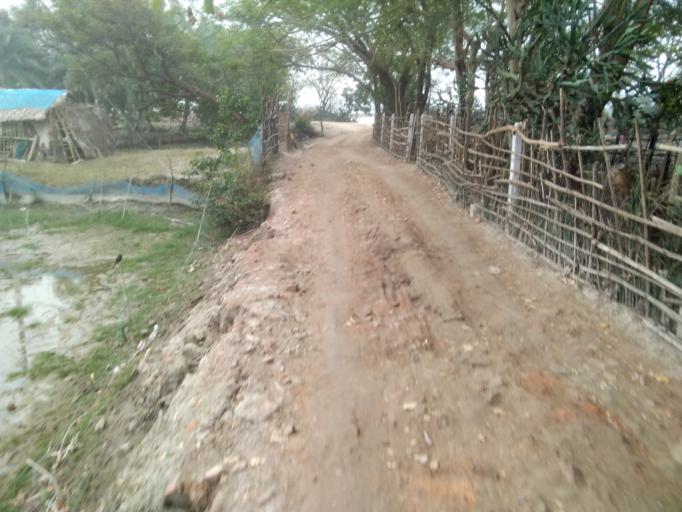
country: BD
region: Khulna
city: Satkhira
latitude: 22.5720
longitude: 89.0770
